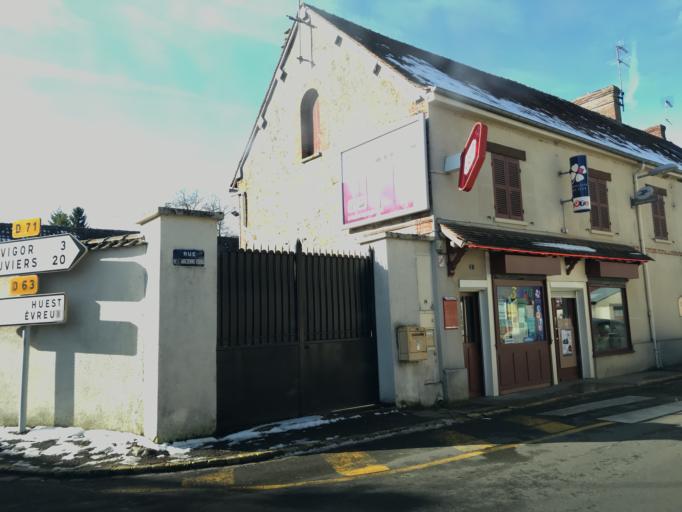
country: FR
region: Haute-Normandie
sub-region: Departement de l'Eure
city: Houlbec-Cocherel
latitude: 49.0671
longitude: 1.2912
